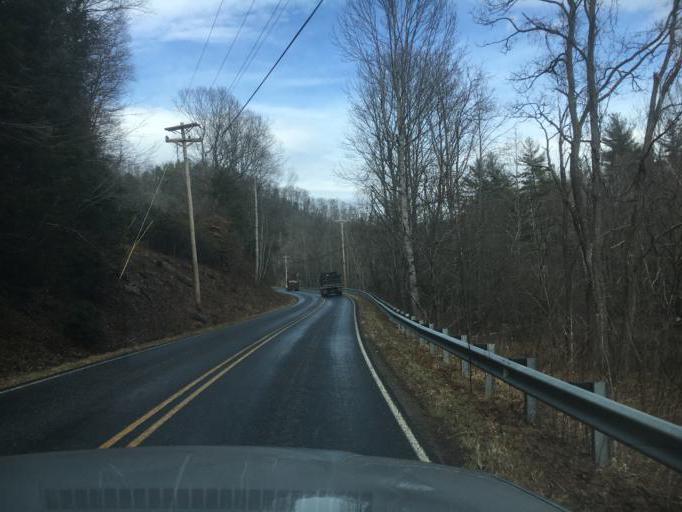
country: US
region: North Carolina
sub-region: Haywood County
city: Canton
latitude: 35.4061
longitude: -82.8135
